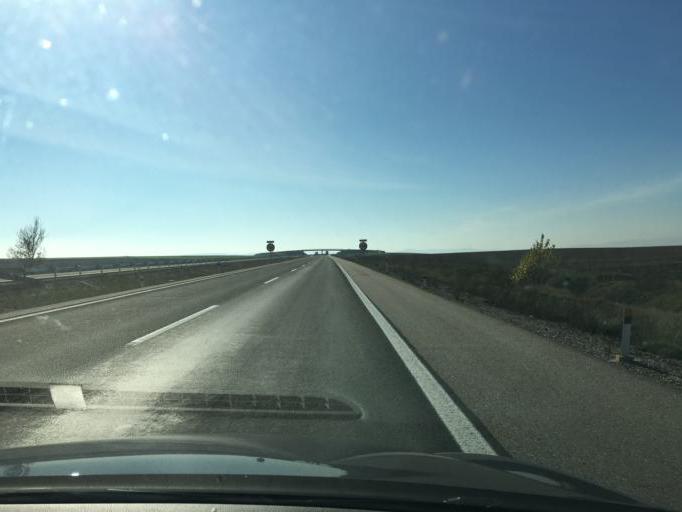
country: ES
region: Castille and Leon
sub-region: Provincia de Burgos
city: Grisalena
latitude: 42.5710
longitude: -3.2610
